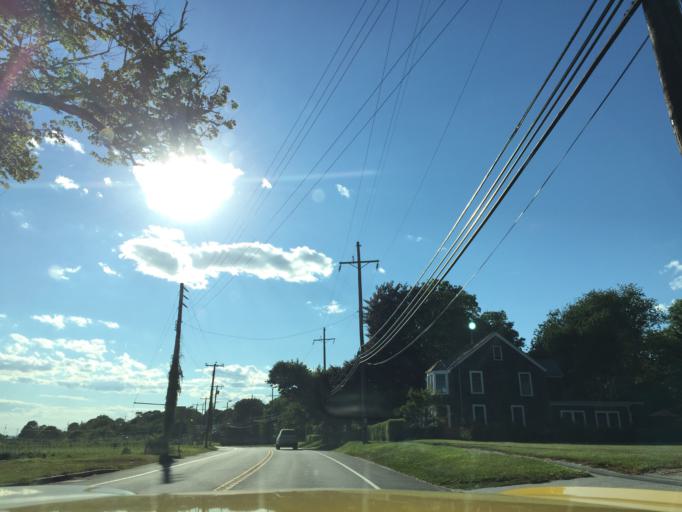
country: US
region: New York
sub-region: Suffolk County
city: Greenport
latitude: 41.1434
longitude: -72.3060
